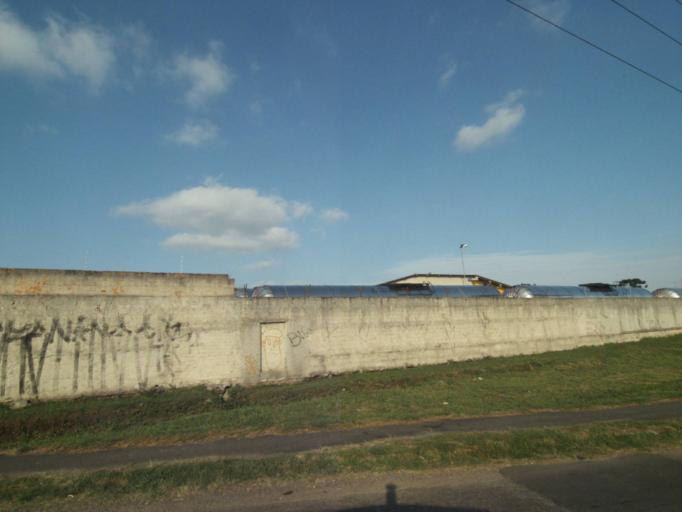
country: BR
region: Parana
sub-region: Curitiba
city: Curitiba
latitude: -25.4889
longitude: -49.3233
